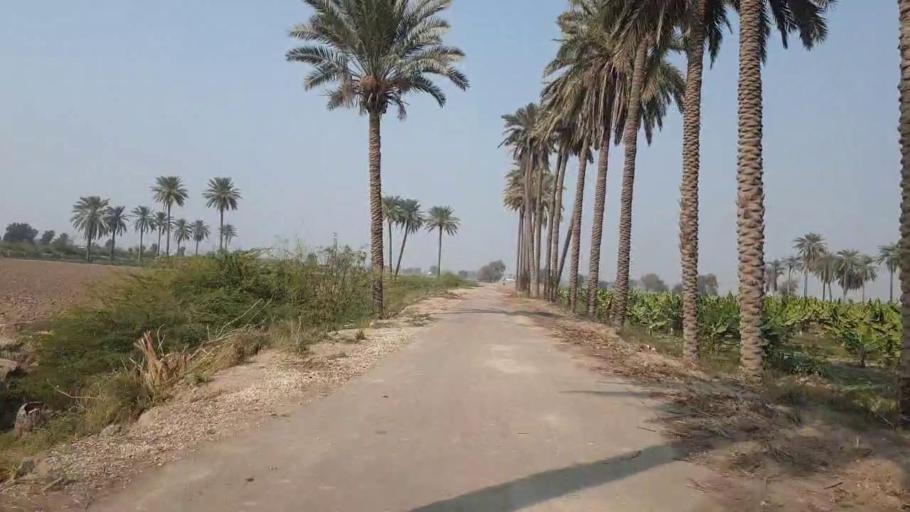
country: PK
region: Sindh
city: Bhit Shah
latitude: 25.7796
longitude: 68.4759
